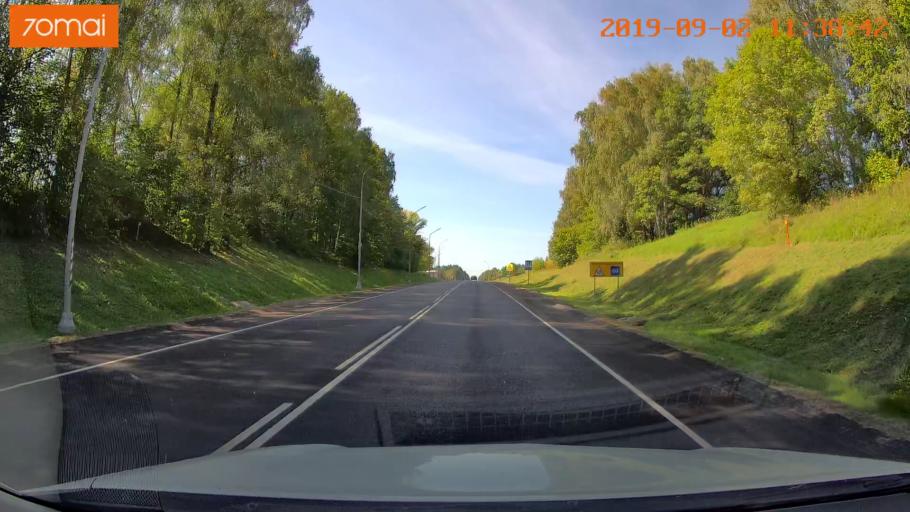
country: RU
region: Smolensk
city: Oster
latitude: 53.9117
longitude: 32.7354
